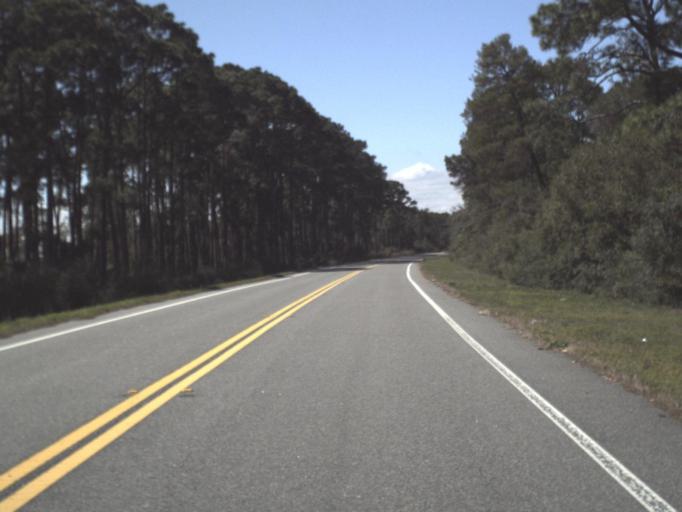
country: US
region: Florida
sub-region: Franklin County
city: Carrabelle
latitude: 29.9276
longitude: -84.4313
